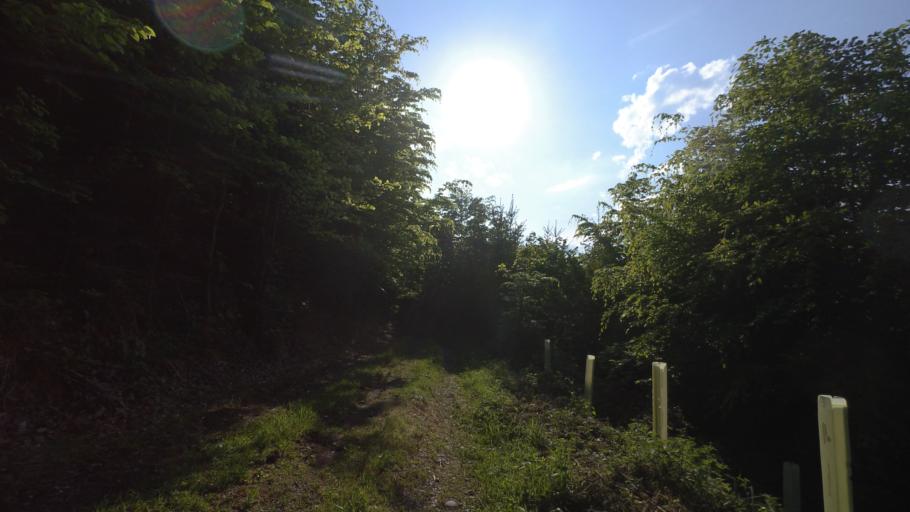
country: DE
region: Bavaria
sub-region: Upper Bavaria
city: Nussdorf
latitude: 47.8959
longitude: 12.5861
